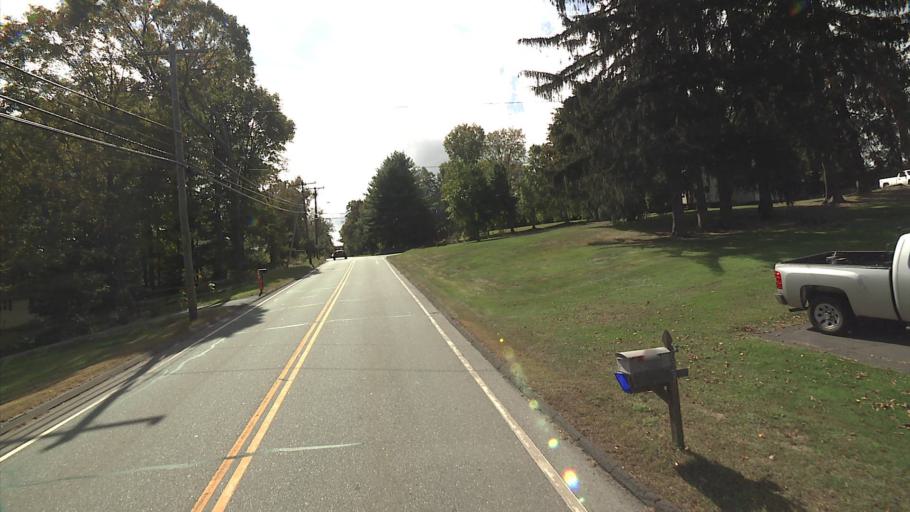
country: US
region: Connecticut
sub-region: Middlesex County
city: Durham
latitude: 41.5038
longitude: -72.7168
